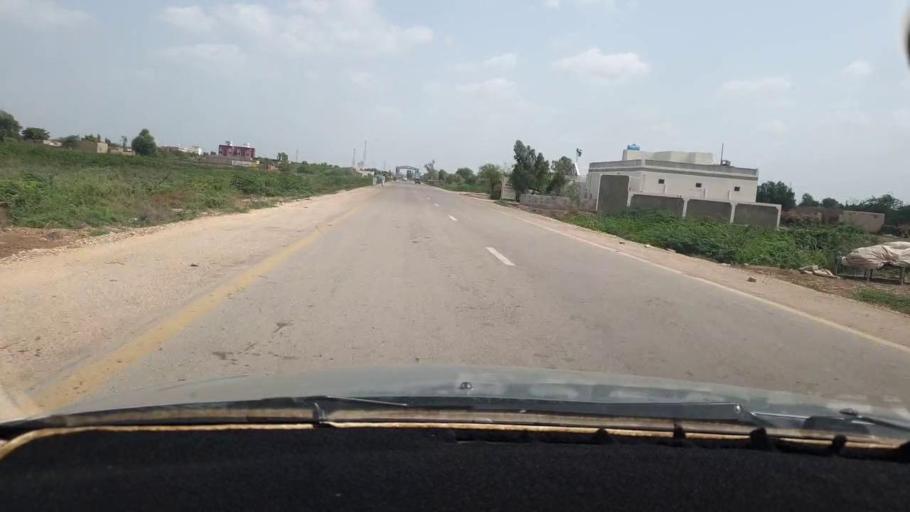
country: PK
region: Sindh
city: Digri
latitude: 25.0856
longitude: 69.2002
